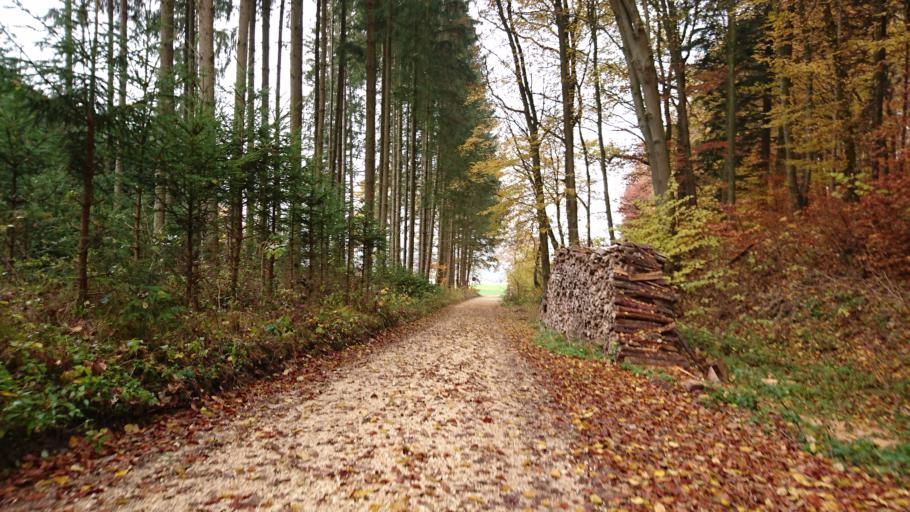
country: DE
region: Bavaria
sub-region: Swabia
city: Altenmunster
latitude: 48.4348
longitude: 10.6086
